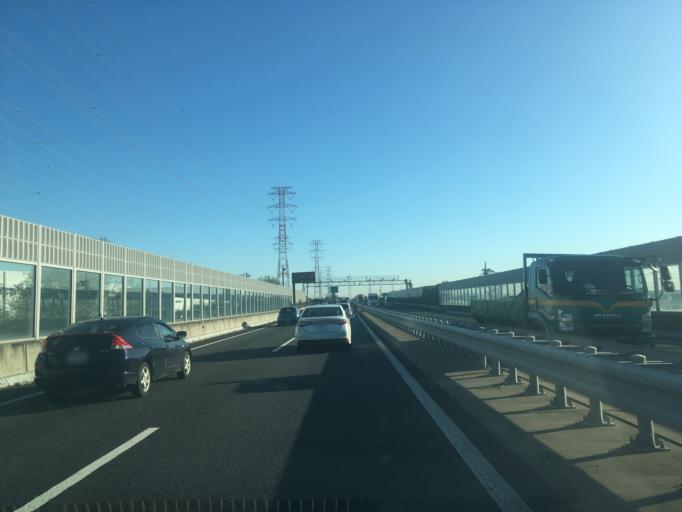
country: JP
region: Saitama
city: Kawagoe
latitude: 35.9793
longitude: 139.4613
